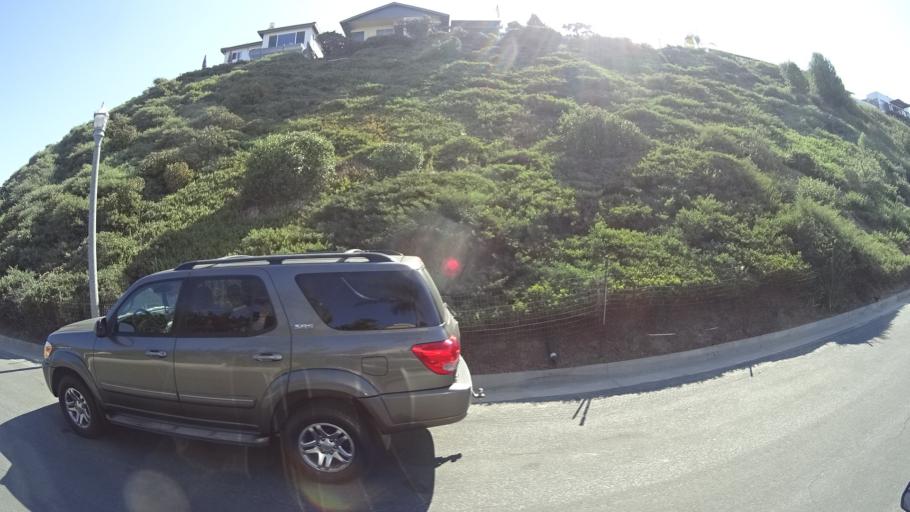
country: US
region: California
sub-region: Orange County
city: San Clemente
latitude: 33.4275
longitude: -117.6046
